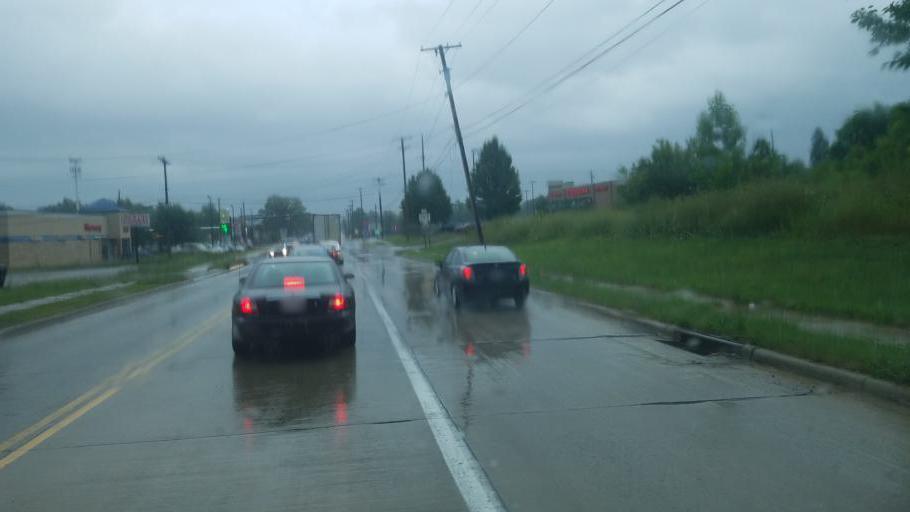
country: US
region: Ohio
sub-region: Trumbull County
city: Churchill
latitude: 41.1336
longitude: -80.6676
